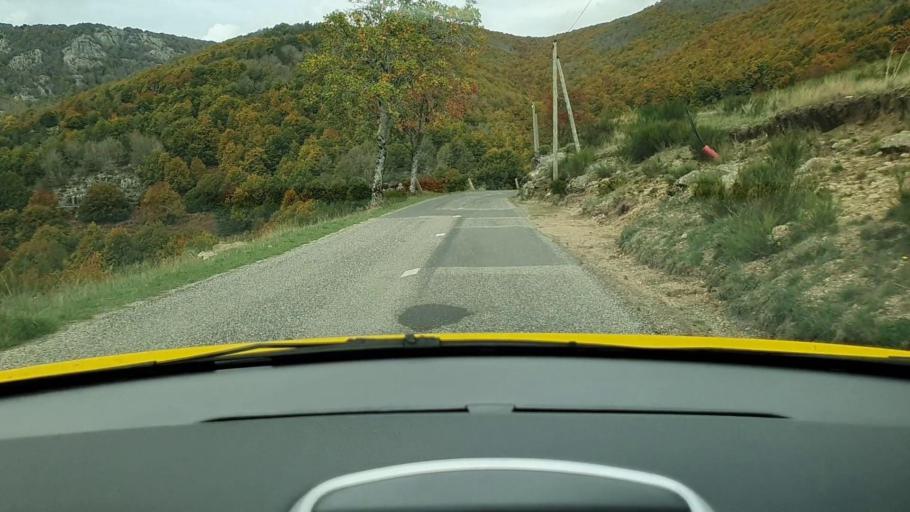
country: FR
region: Languedoc-Roussillon
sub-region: Departement du Gard
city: Le Vigan
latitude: 44.0734
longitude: 3.5160
